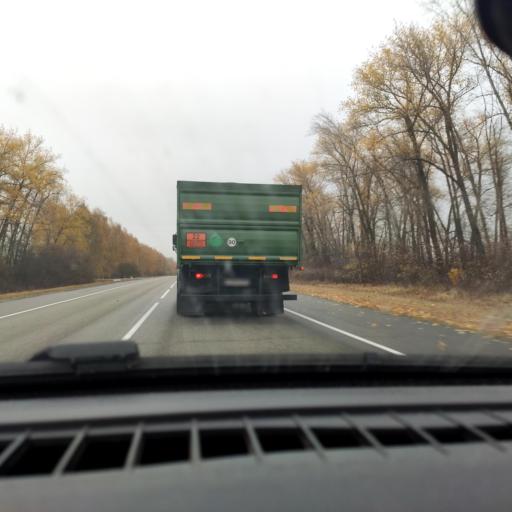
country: RU
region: Voronezj
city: Ostrogozhsk
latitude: 50.9918
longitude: 38.9982
